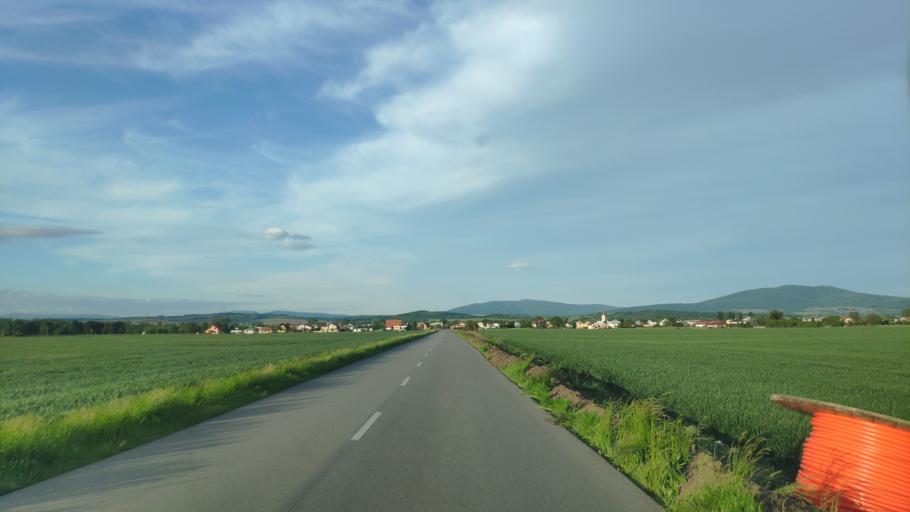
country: SK
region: Kosicky
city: Kosice
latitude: 48.6450
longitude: 21.3117
